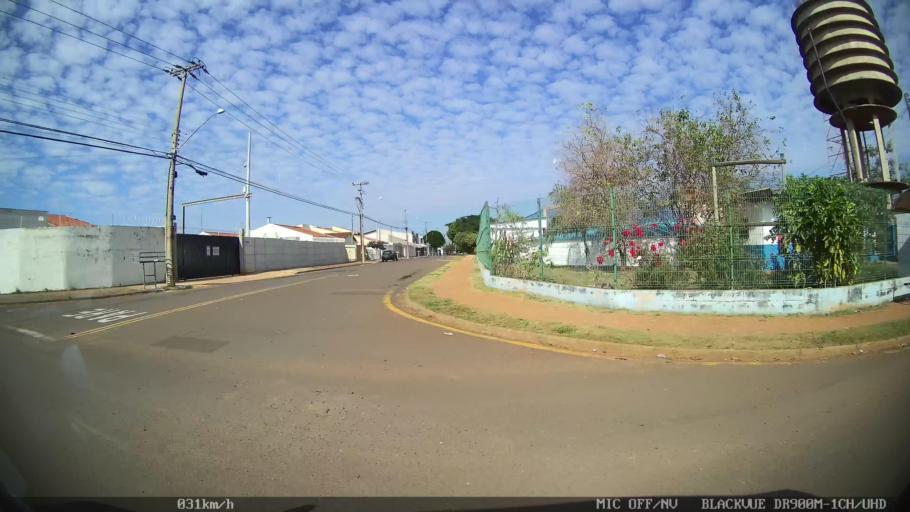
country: BR
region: Sao Paulo
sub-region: Santa Barbara D'Oeste
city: Santa Barbara d'Oeste
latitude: -22.7625
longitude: -47.3976
